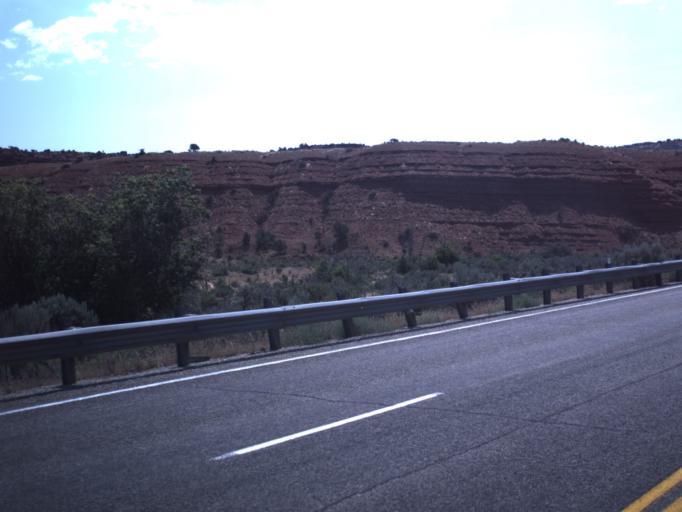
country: US
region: Utah
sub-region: Uintah County
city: Vernal
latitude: 40.5999
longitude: -109.4659
